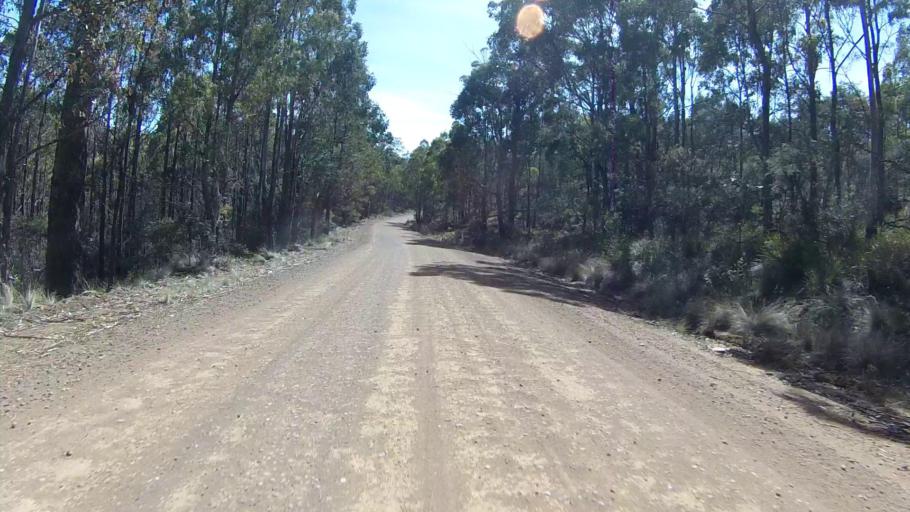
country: AU
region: Tasmania
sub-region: Sorell
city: Sorell
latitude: -42.6718
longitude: 147.7266
